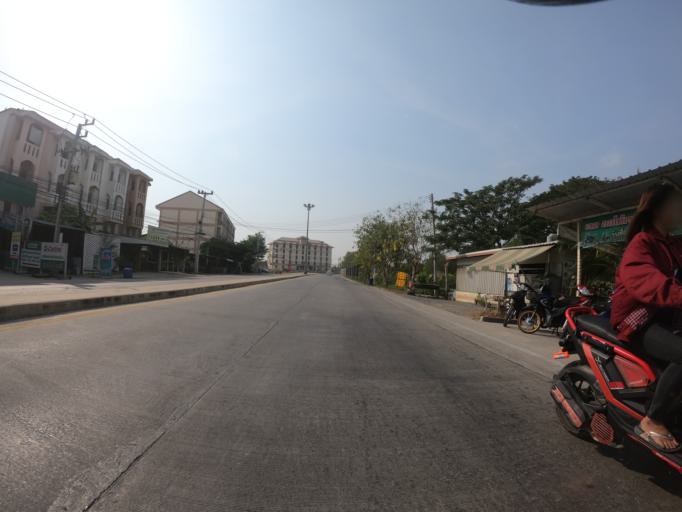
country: TH
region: Phra Nakhon Si Ayutthaya
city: Phra Nakhon Si Ayutthaya
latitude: 14.3409
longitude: 100.5936
